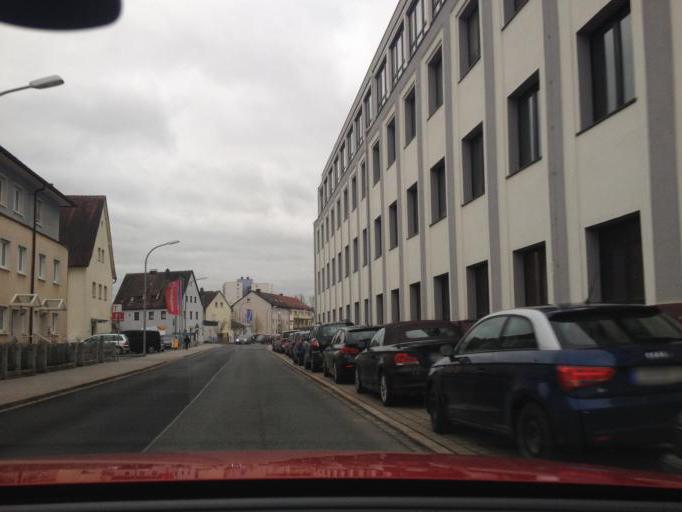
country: DE
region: Bavaria
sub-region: Regierungsbezirk Mittelfranken
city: Lauf an der Pegnitz
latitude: 49.5065
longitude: 11.2800
